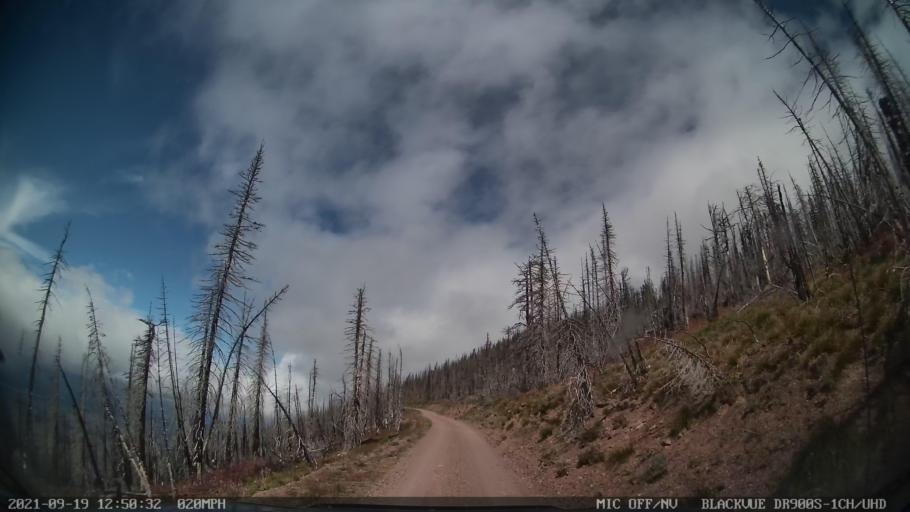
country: US
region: Montana
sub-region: Missoula County
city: Seeley Lake
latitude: 47.1858
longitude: -113.3572
